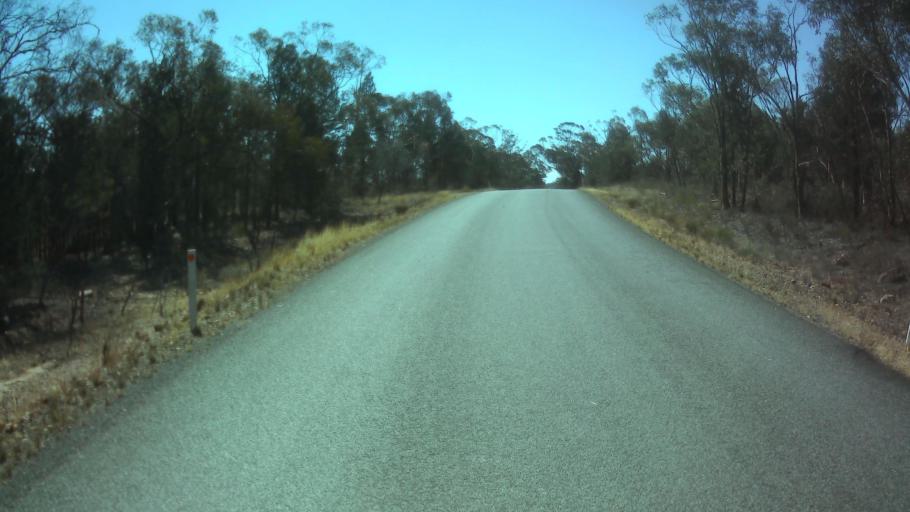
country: AU
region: New South Wales
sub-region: Weddin
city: Grenfell
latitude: -33.8054
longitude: 147.8979
